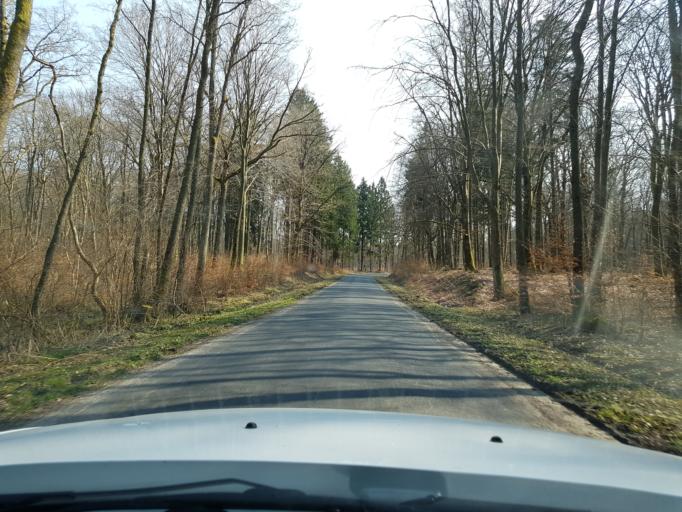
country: PL
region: West Pomeranian Voivodeship
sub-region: Powiat koszalinski
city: Sianow
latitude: 54.2619
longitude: 16.3125
